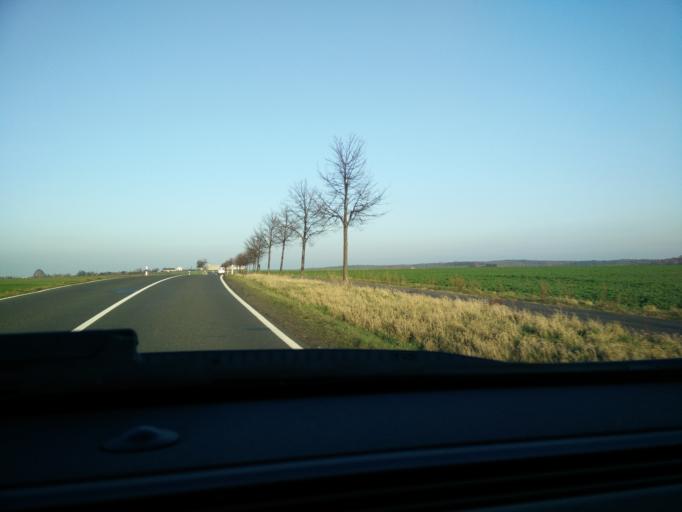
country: DE
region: Saxony
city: Grossbardau
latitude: 51.1885
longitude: 12.6939
